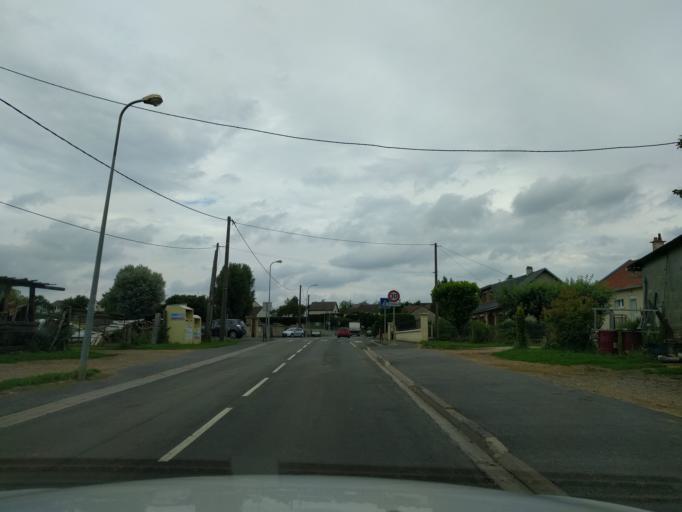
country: FR
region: Champagne-Ardenne
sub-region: Departement des Ardennes
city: Warcq
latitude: 49.7740
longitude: 4.6800
